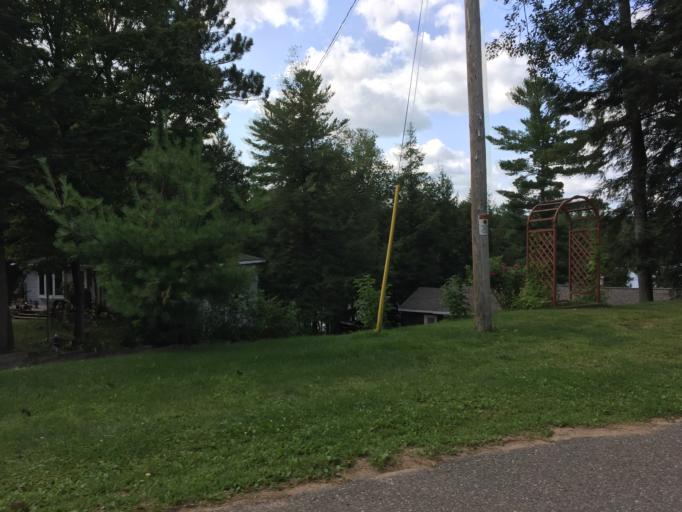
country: US
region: Wisconsin
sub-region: Menominee County
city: Legend Lake
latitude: 45.3129
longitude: -88.4770
